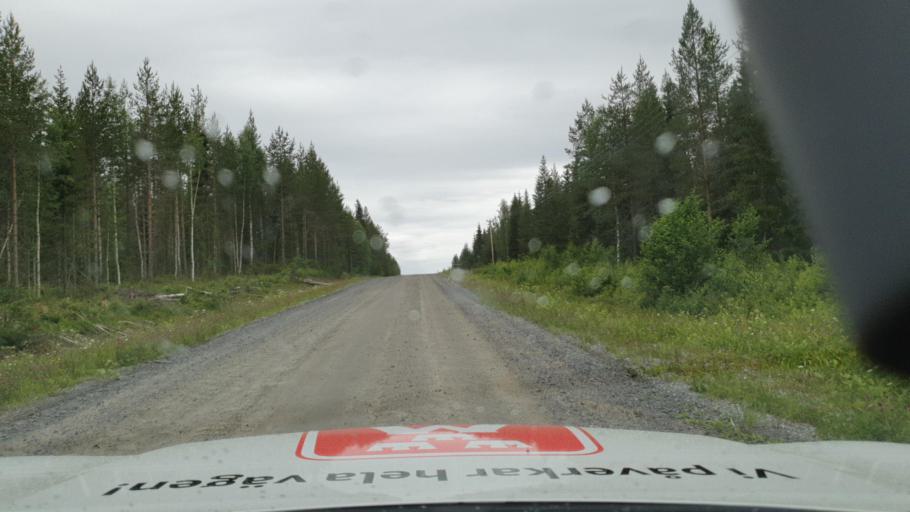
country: SE
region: Vaesterbotten
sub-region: Nordmalings Kommun
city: Nordmaling
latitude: 63.7572
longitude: 19.4903
